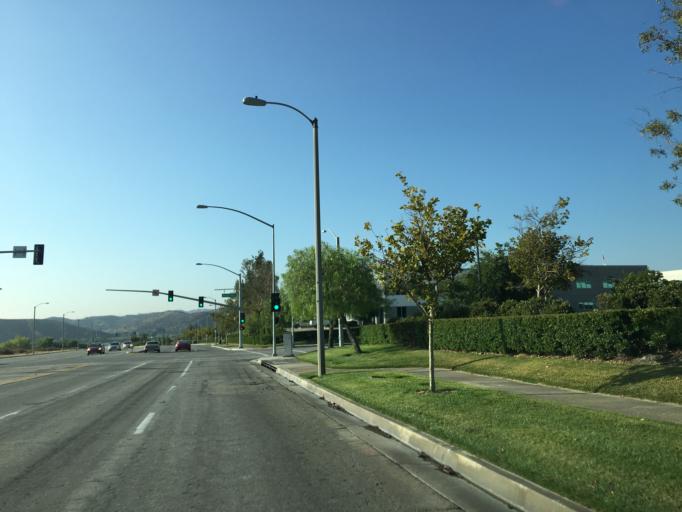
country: US
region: California
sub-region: Los Angeles County
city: Valencia
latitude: 34.4418
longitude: -118.6249
